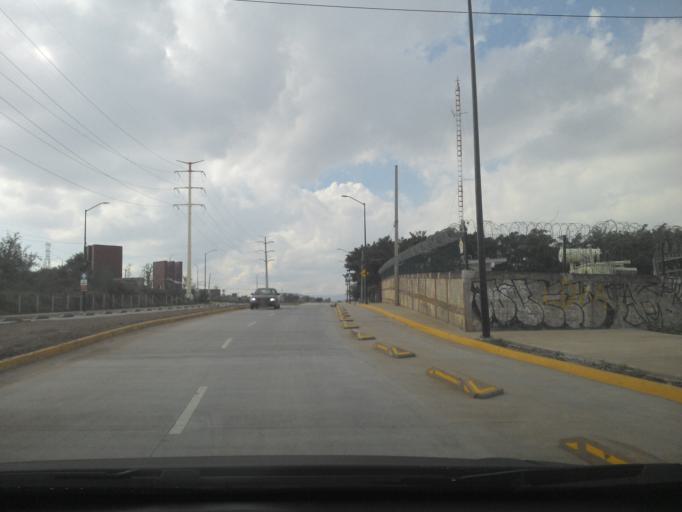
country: MX
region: Jalisco
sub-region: Tlajomulco de Zuniga
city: Altus Bosques
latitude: 20.6148
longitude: -103.3612
